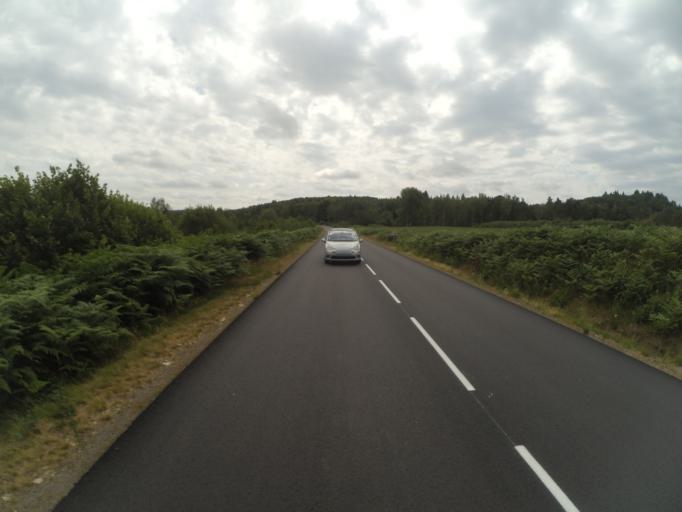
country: FR
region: Limousin
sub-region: Departement de la Creuse
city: La Courtine
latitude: 45.6547
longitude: 2.2379
